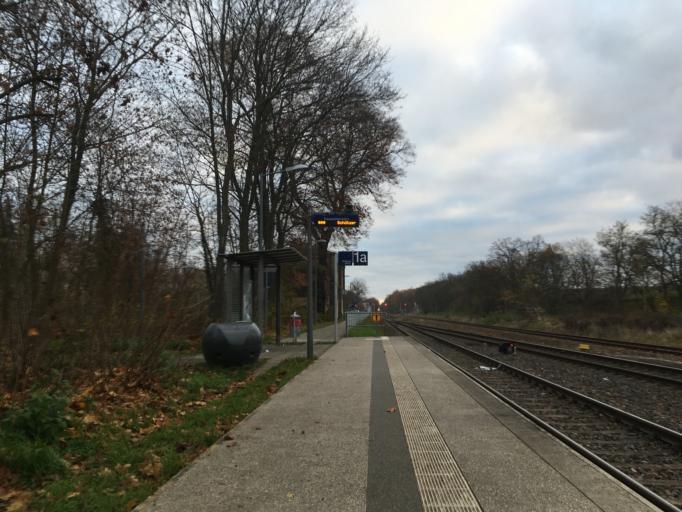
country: DE
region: Brandenburg
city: Seelow
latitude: 52.5591
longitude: 14.3501
